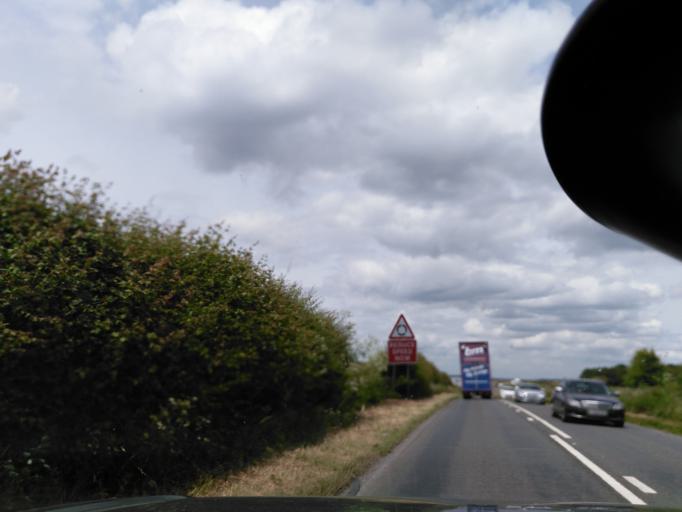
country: GB
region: England
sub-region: Wiltshire
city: Winterbourne Stoke
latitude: 51.1691
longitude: -1.8591
